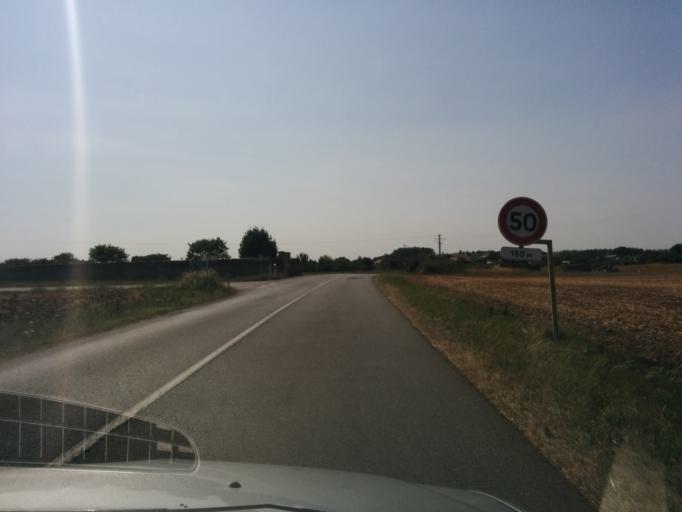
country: FR
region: Poitou-Charentes
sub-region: Departement de la Vienne
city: Saint-Jean-de-Sauves
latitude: 46.8053
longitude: 0.0243
